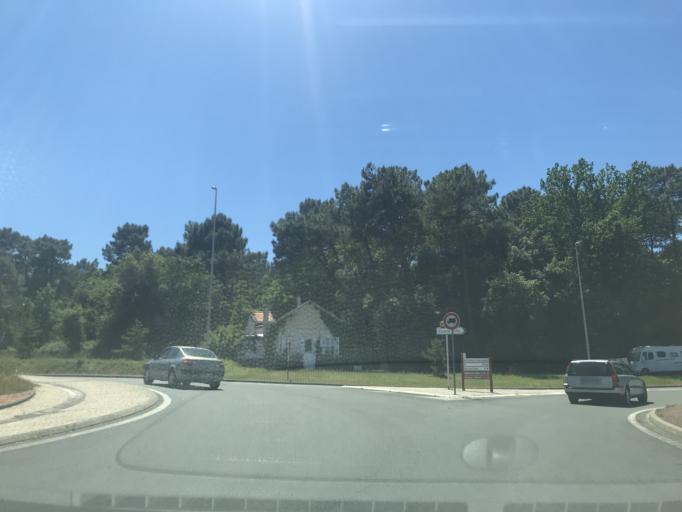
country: FR
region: Poitou-Charentes
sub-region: Departement de la Charente-Maritime
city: Saint-Georges-de-Didonne
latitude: 45.5967
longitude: -0.9751
